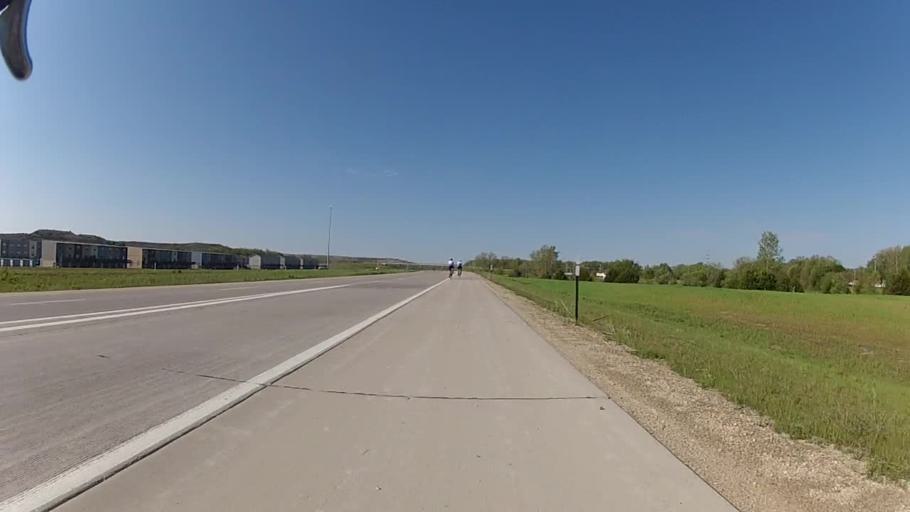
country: US
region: Kansas
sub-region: Riley County
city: Ogden
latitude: 39.1110
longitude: -96.6992
